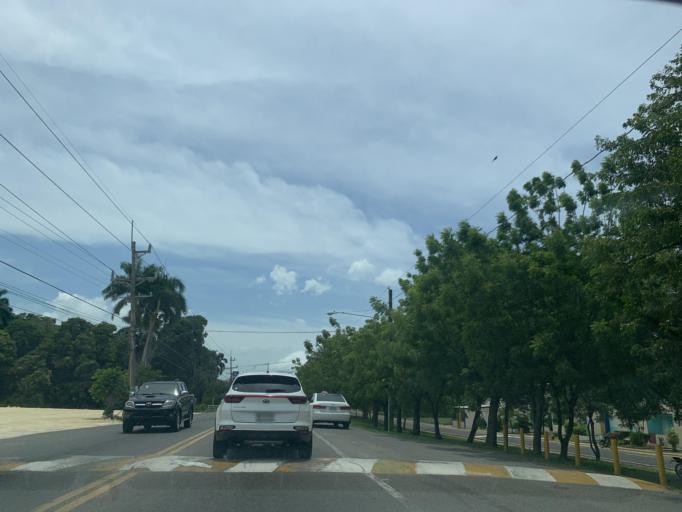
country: DO
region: Puerto Plata
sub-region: Puerto Plata
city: Puerto Plata
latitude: 19.7503
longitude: -70.5738
